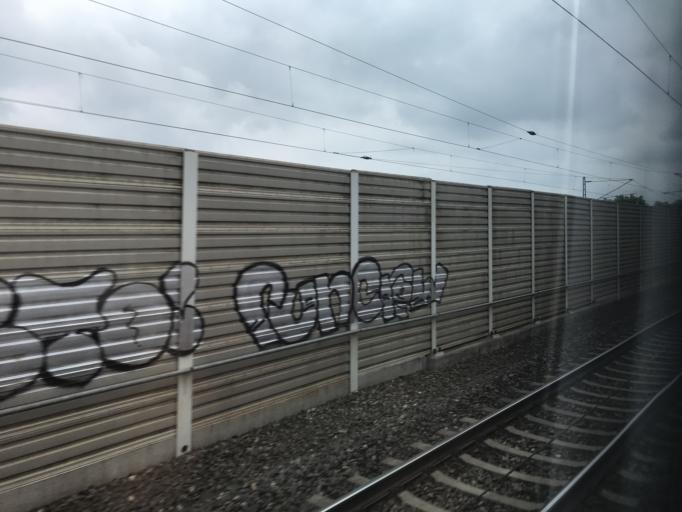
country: DE
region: Bavaria
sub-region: Swabia
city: Augsburg
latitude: 48.3536
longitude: 10.9307
